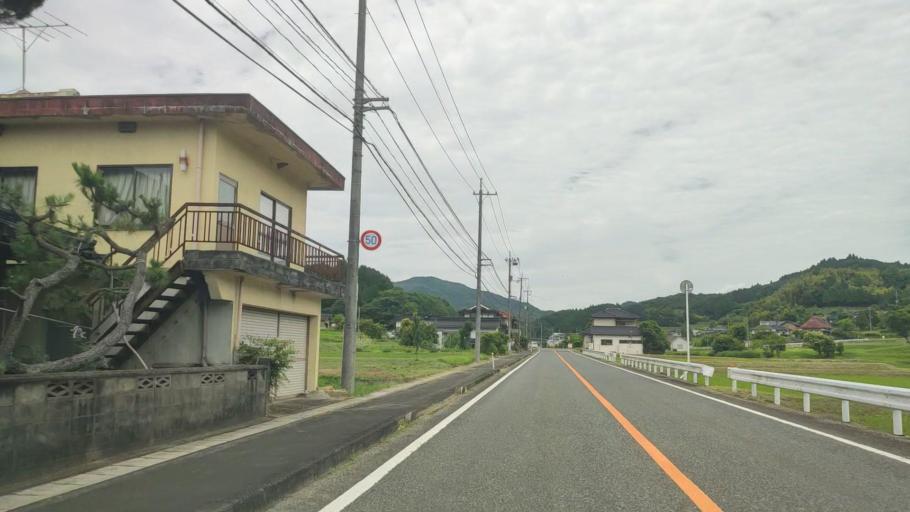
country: JP
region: Okayama
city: Tsuyama
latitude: 35.0709
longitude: 134.2402
